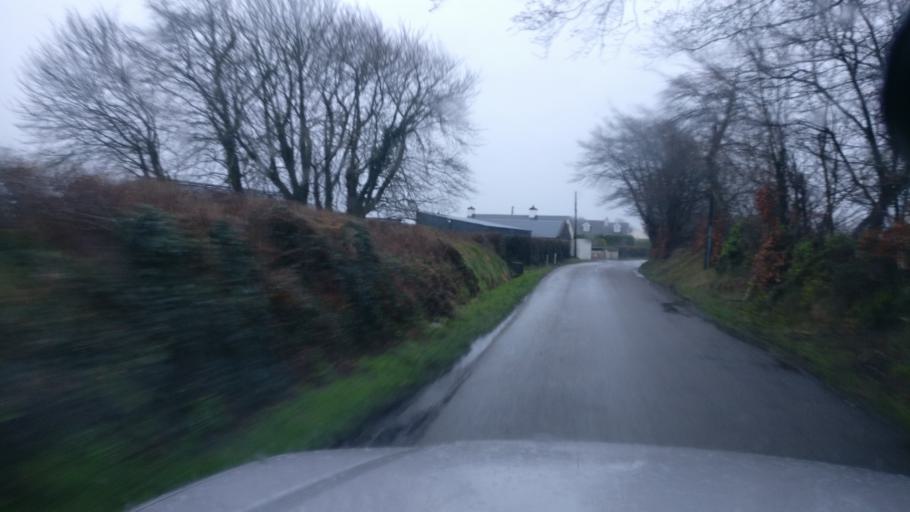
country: IE
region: Connaught
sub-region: County Galway
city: Ballinasloe
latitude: 53.3145
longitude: -8.3681
